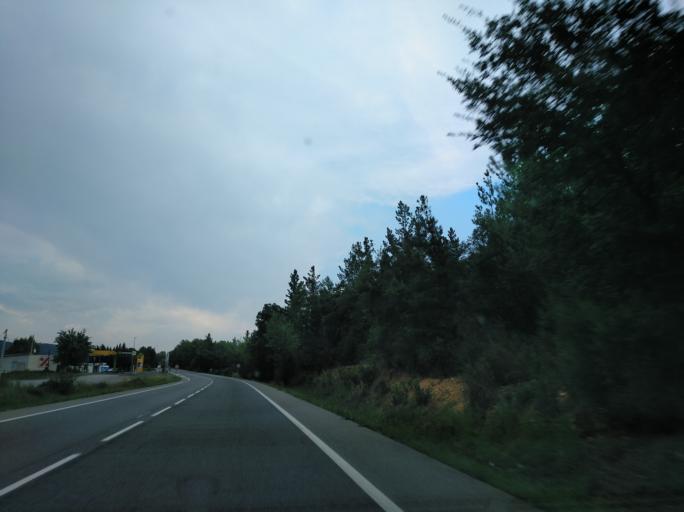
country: ES
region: Catalonia
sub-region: Provincia de Girona
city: Santa Coloma de Farners
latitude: 41.8842
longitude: 2.6581
